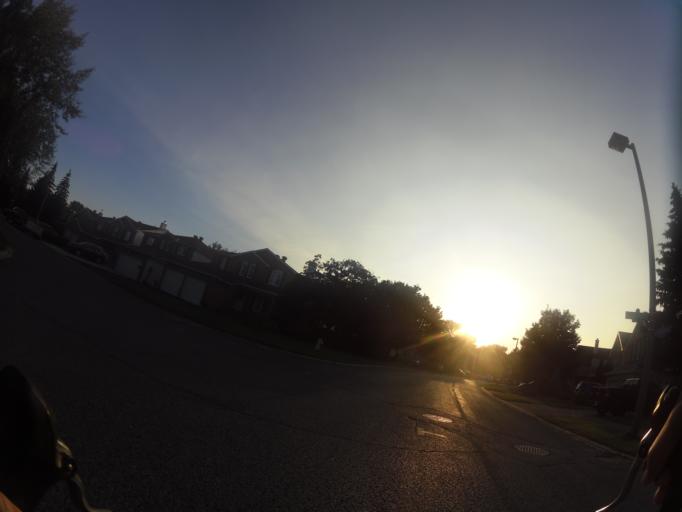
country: CA
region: Ontario
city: Bells Corners
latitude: 45.3458
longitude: -75.9340
